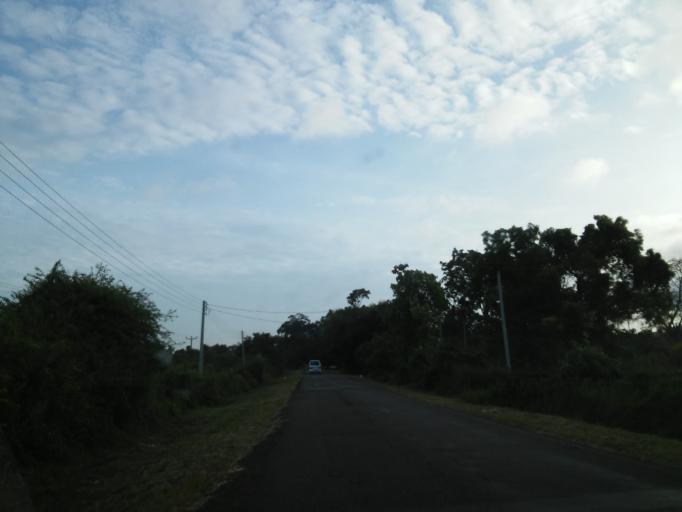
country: LK
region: Central
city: Sigiriya
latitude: 8.1070
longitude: 80.6325
